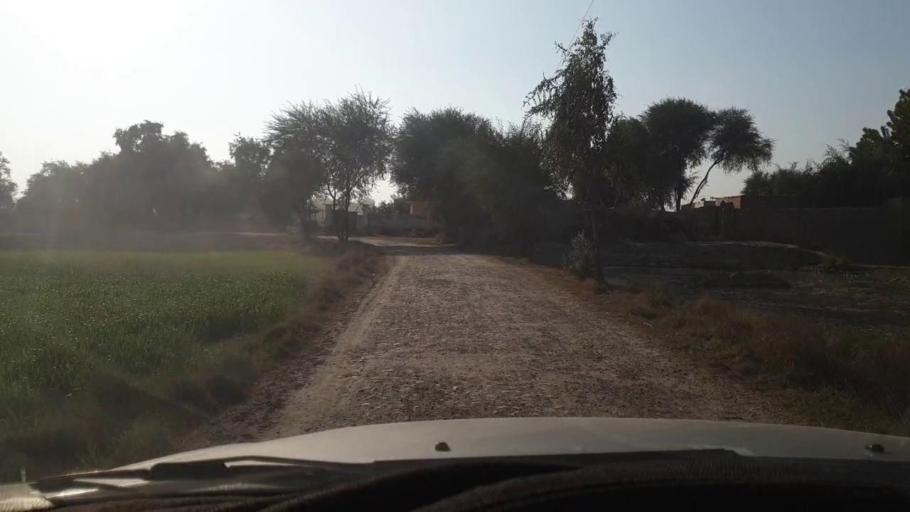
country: PK
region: Sindh
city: Mirpur Mathelo
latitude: 28.0176
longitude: 69.6002
